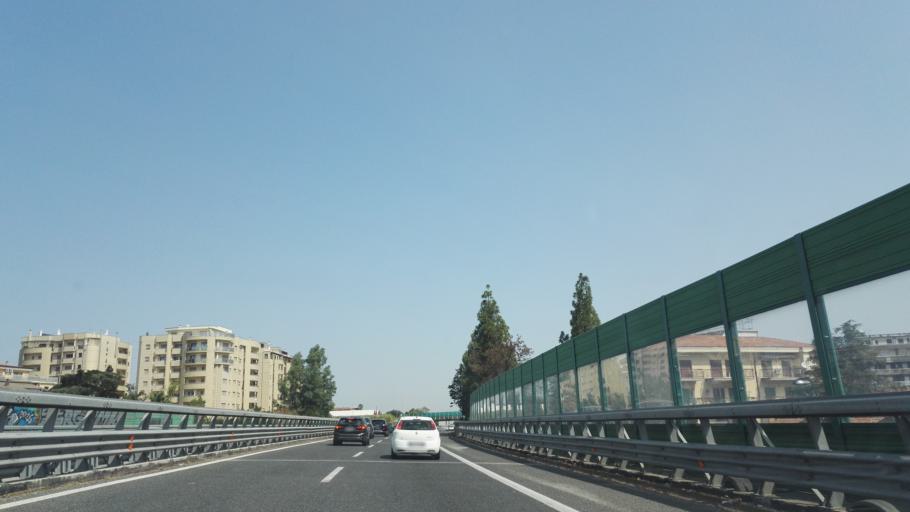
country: IT
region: Calabria
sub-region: Provincia di Cosenza
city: Cosenza
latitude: 39.3222
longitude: 16.2401
